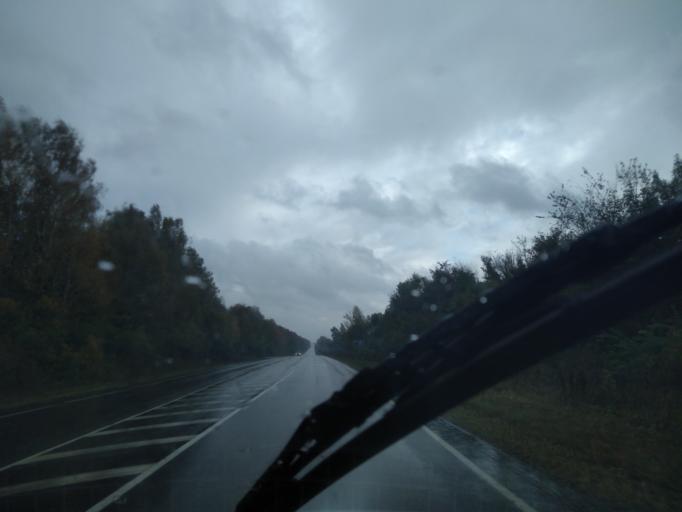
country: RU
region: Tula
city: Teploye
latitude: 53.5204
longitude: 37.6850
